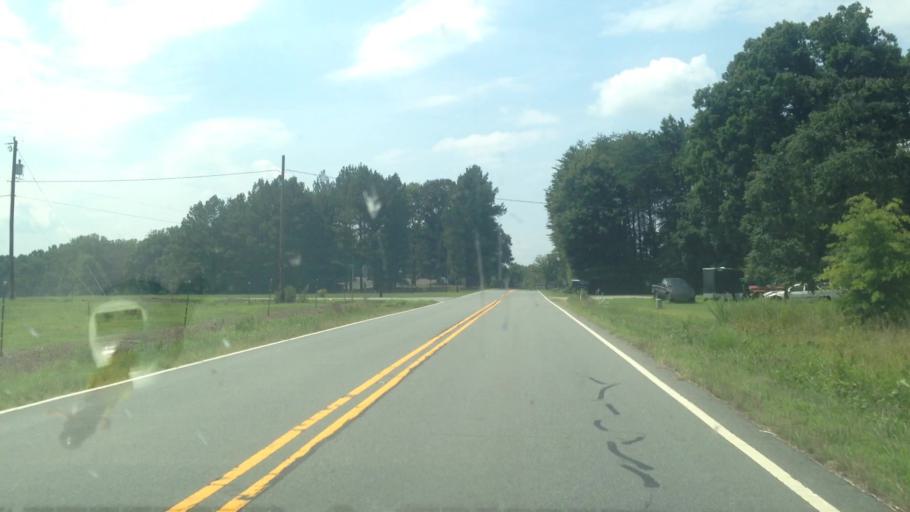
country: US
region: North Carolina
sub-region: Stokes County
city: Walnut Cove
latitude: 36.3540
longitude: -80.0588
